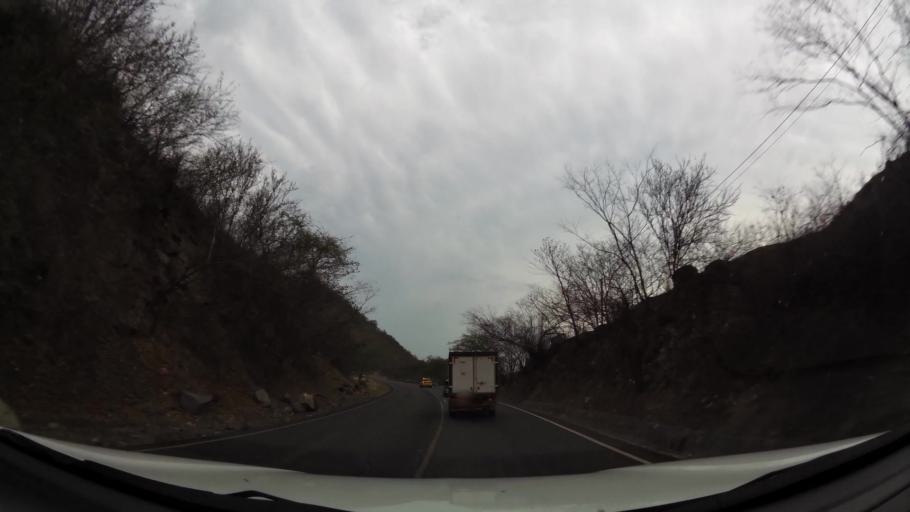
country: NI
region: Esteli
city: Esteli
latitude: 12.9438
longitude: -86.2186
